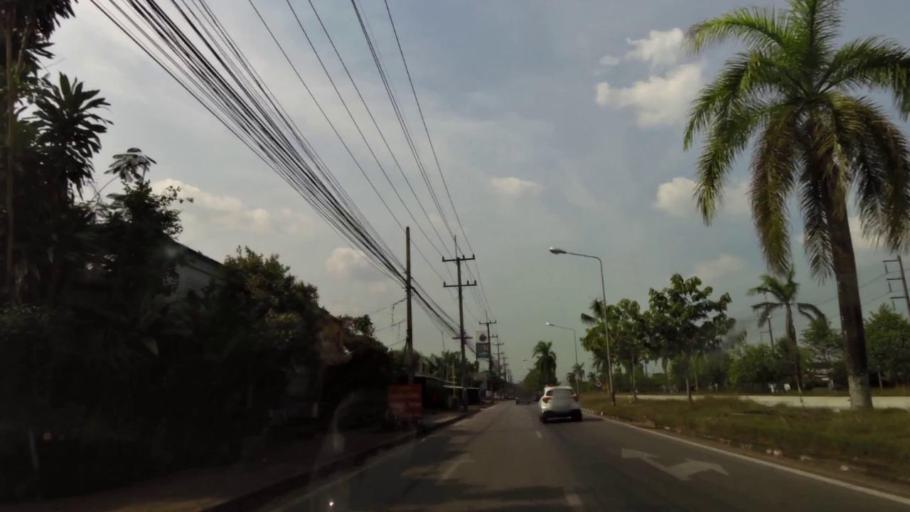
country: TH
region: Rayong
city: Klaeng
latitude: 12.7916
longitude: 101.6464
